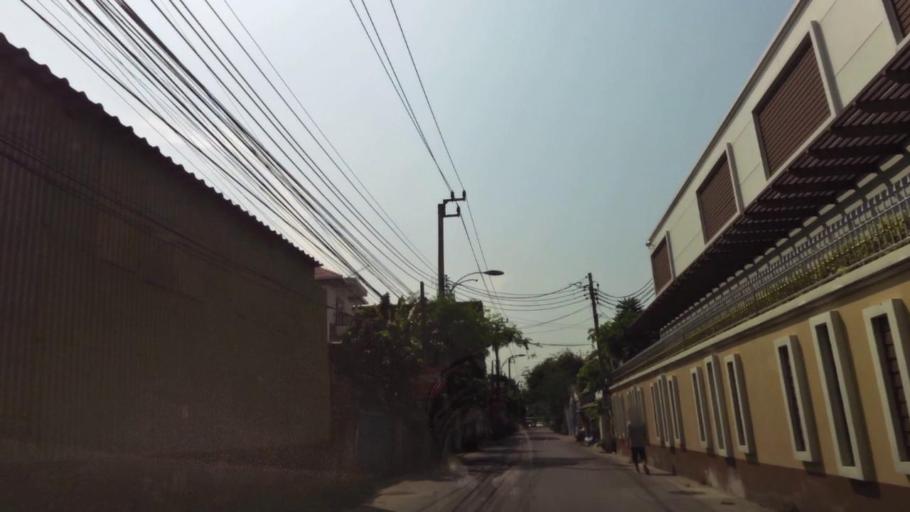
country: TH
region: Bangkok
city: Phra Khanong
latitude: 13.6561
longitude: 100.5963
